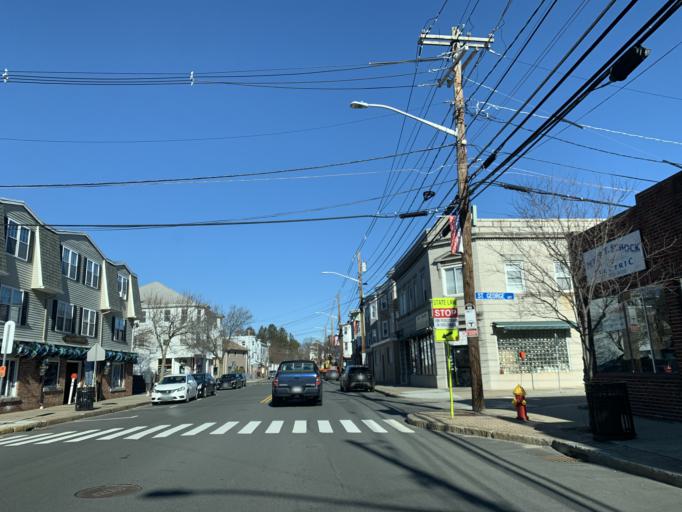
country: US
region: Massachusetts
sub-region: Norfolk County
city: Norwood
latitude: 42.1778
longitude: -71.2061
